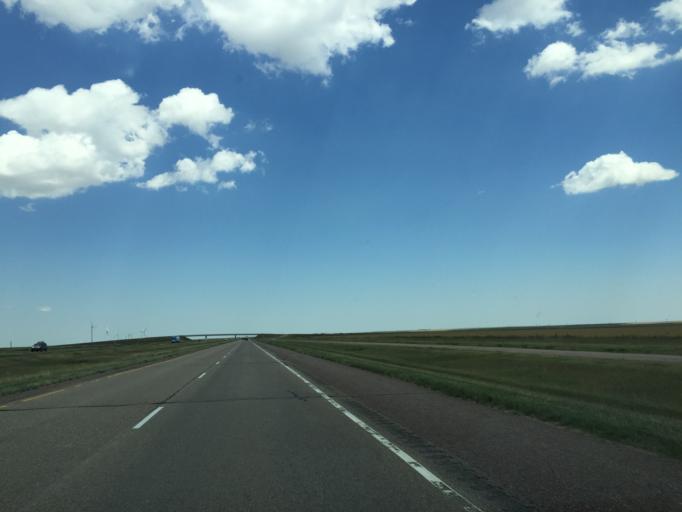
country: US
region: Colorado
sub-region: Lincoln County
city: Hugo
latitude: 39.2776
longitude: -103.4471
